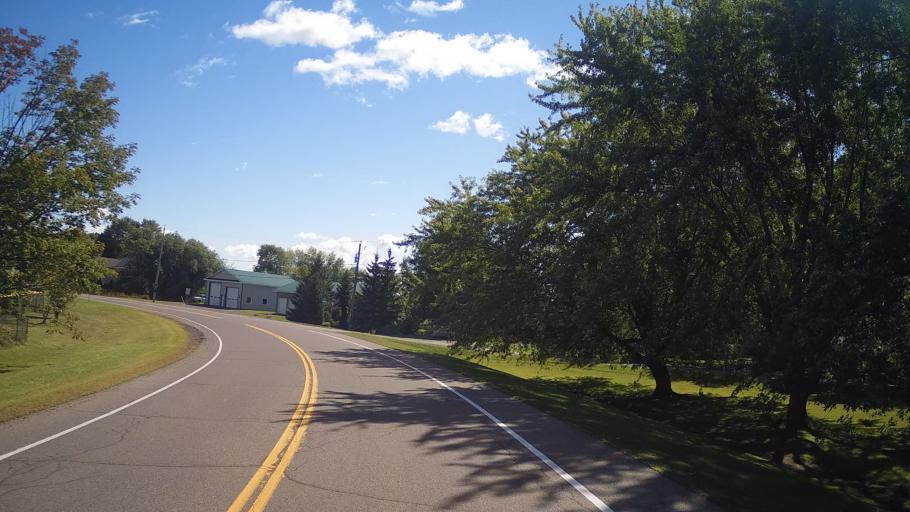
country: US
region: New York
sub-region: St. Lawrence County
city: Norfolk
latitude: 44.9711
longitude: -75.2514
